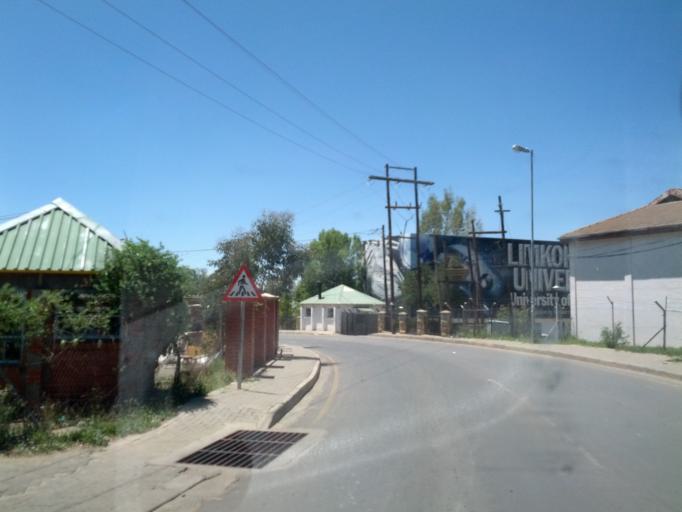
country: LS
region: Maseru
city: Maseru
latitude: -29.3063
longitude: 27.4866
